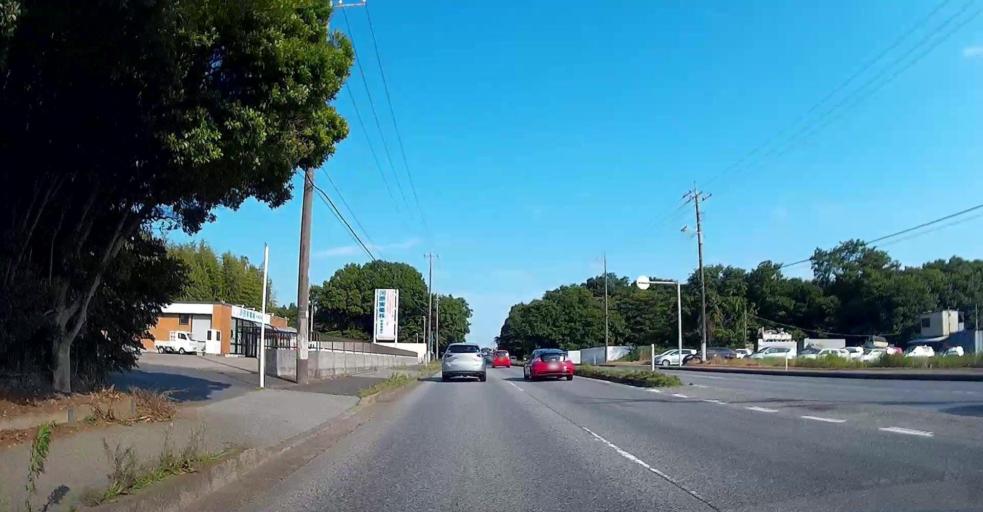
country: JP
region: Chiba
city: Shiroi
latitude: 35.7763
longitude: 140.0882
